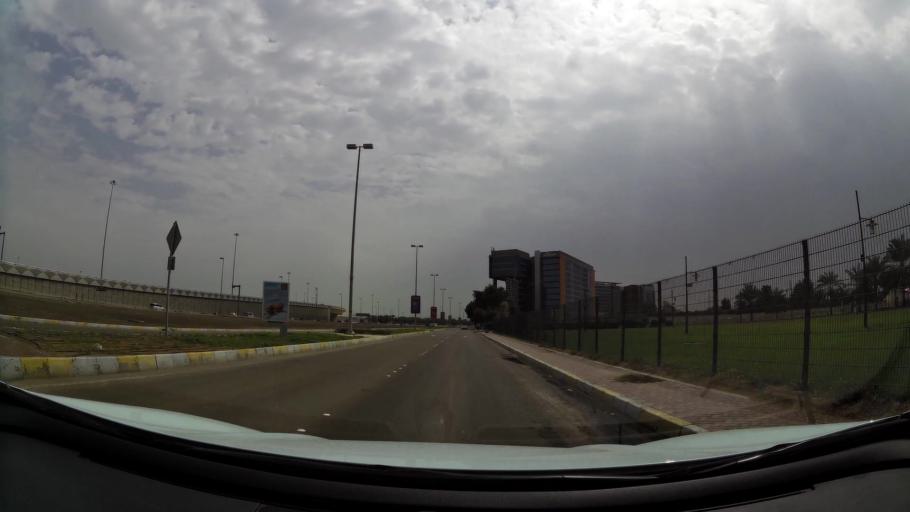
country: AE
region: Abu Dhabi
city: Abu Dhabi
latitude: 24.4277
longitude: 54.4705
